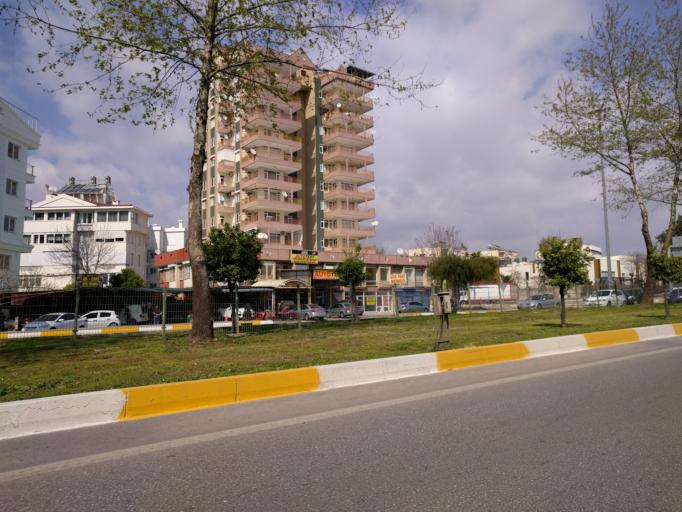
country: TR
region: Antalya
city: Antalya
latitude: 36.9008
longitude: 30.6619
